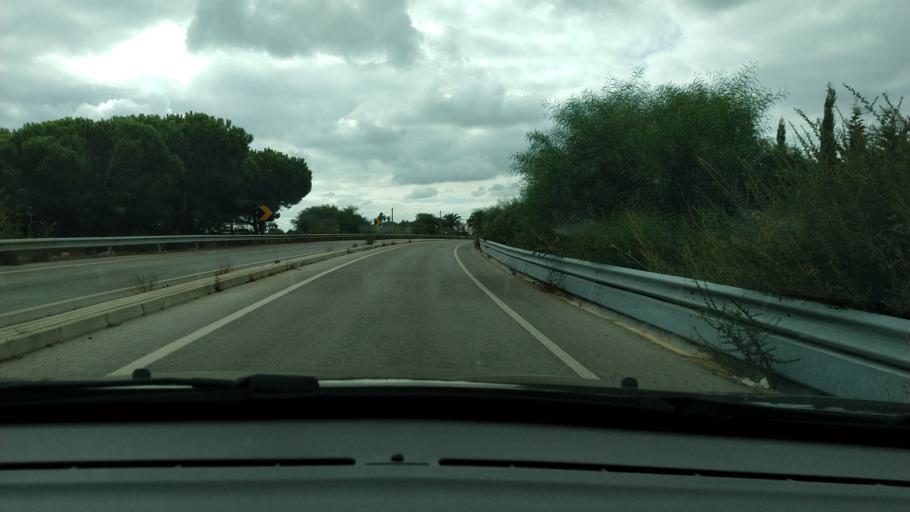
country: PT
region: Faro
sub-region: Lagos
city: Lagos
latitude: 37.0978
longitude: -8.7398
